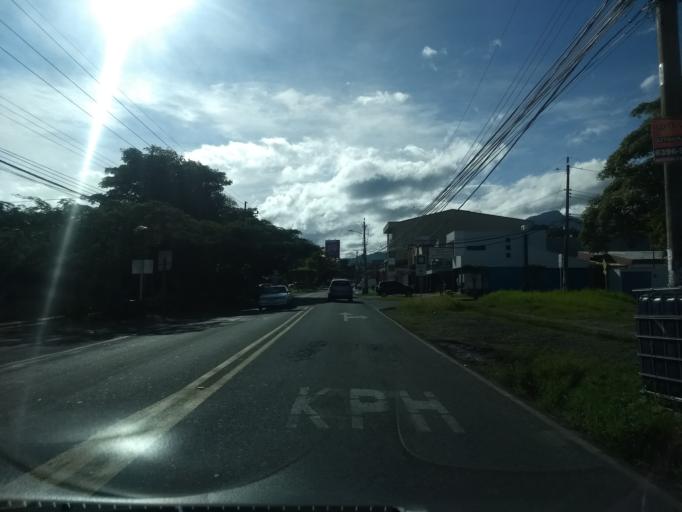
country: CR
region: San Jose
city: San Rafael
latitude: 9.9392
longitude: -84.1540
